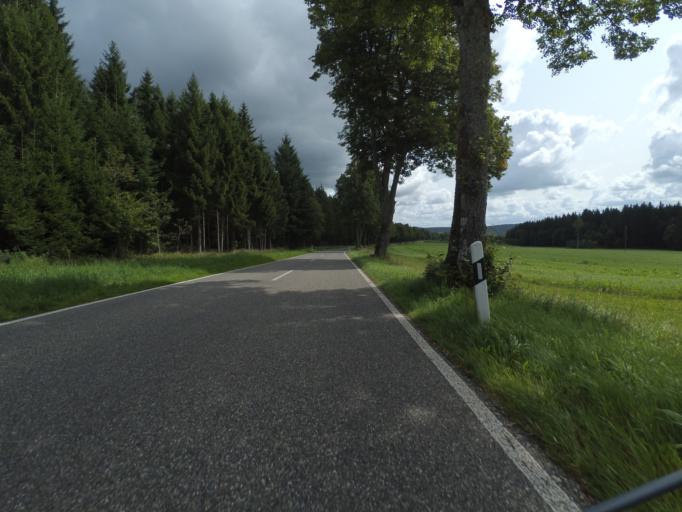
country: DE
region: Baden-Wuerttemberg
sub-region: Freiburg Region
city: Braunlingen
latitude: 47.9652
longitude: 8.4053
